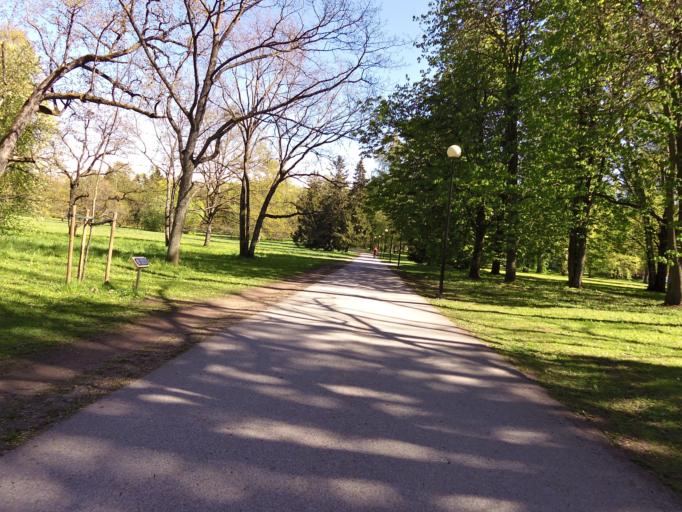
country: EE
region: Harju
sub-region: Tallinna linn
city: Tallinn
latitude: 59.4388
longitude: 24.7946
